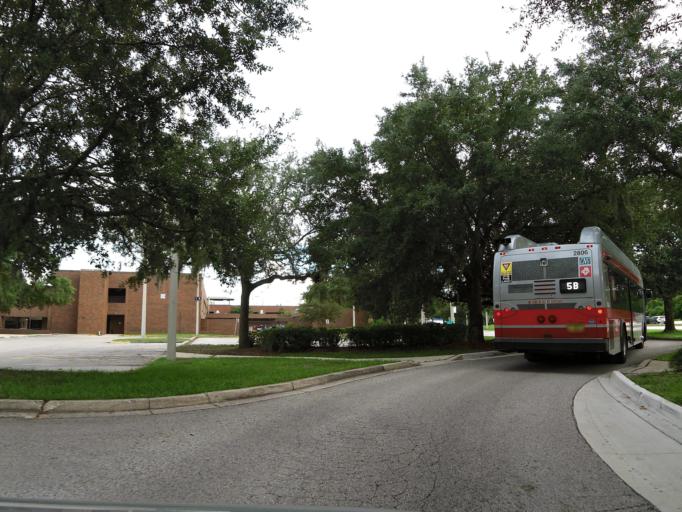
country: US
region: Florida
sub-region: Duval County
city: Jacksonville
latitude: 30.3024
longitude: -81.7194
